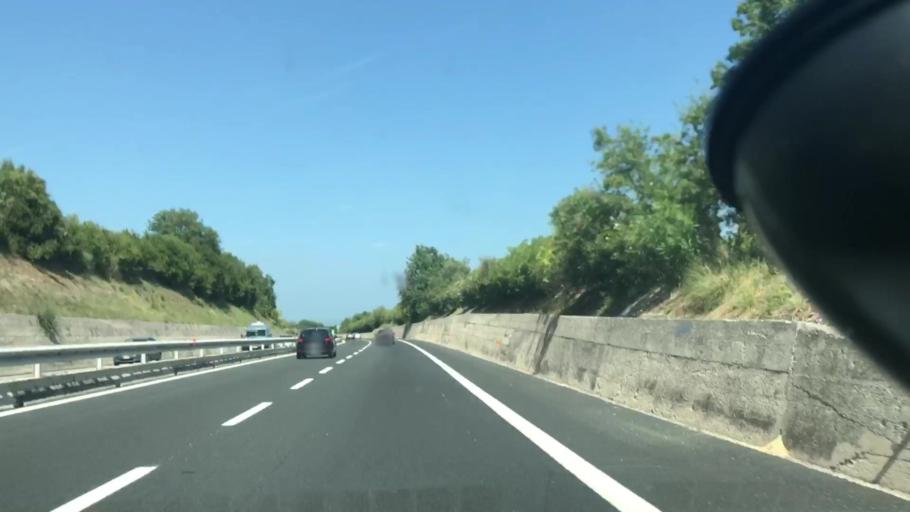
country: IT
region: Abruzzo
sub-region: Provincia di Chieti
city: Ortona
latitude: 42.3437
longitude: 14.3579
